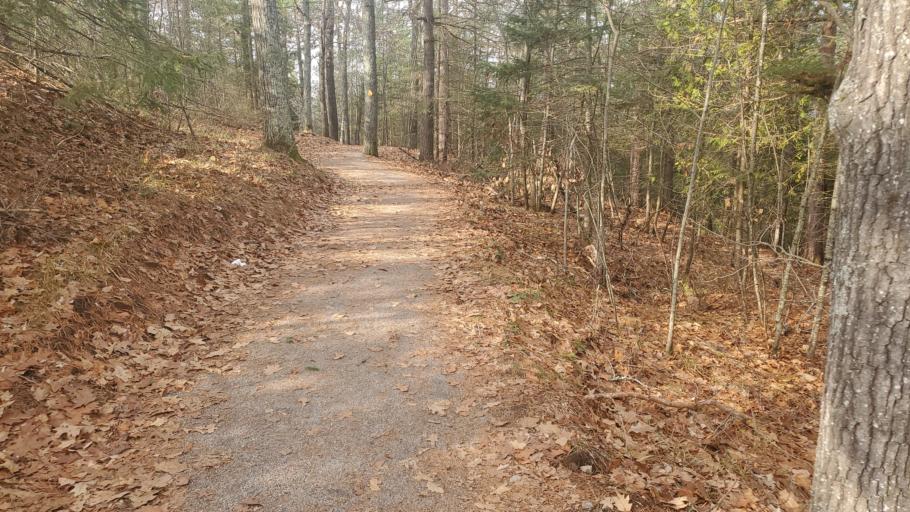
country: CA
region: Ontario
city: Bancroft
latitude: 45.0734
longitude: -77.8575
